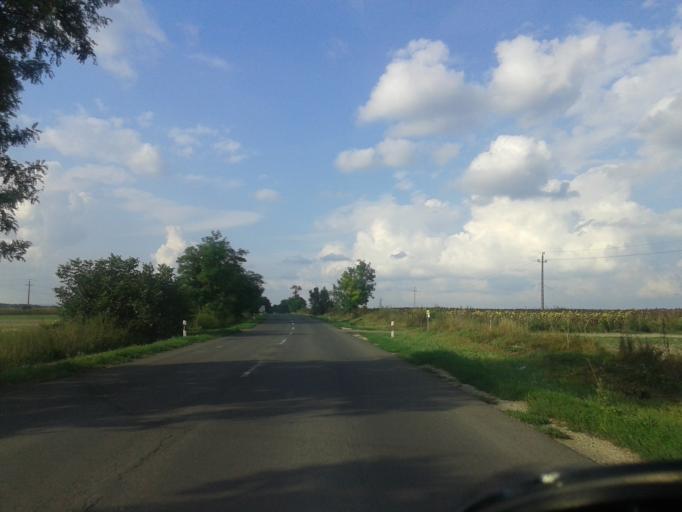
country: HU
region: Pest
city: Kiskunlachaza
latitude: 47.2198
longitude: 19.0197
